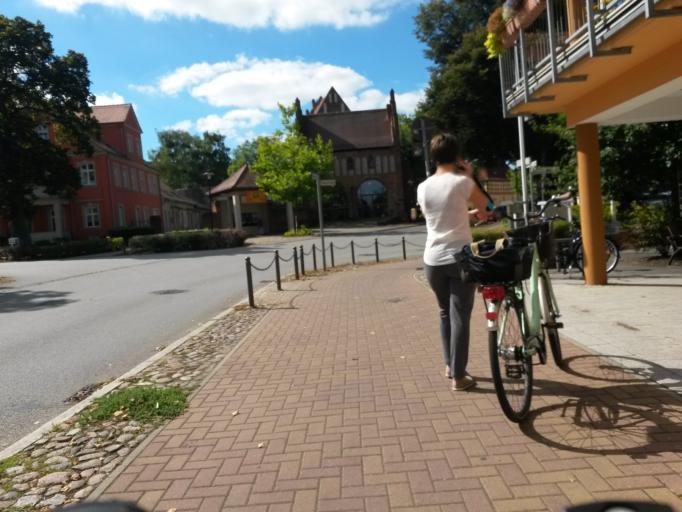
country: DE
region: Brandenburg
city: Templin
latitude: 53.1208
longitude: 13.5049
